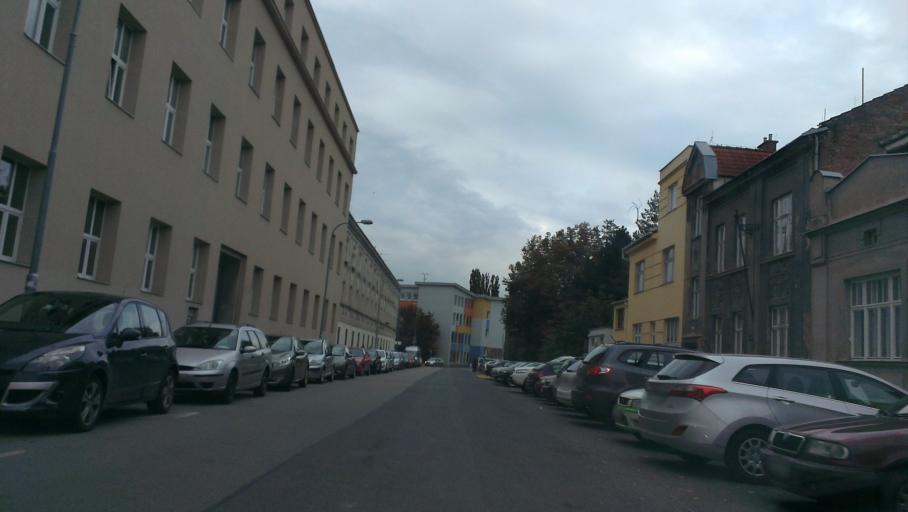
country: CZ
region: South Moravian
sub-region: Mesto Brno
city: Brno
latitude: 49.1847
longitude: 16.5965
